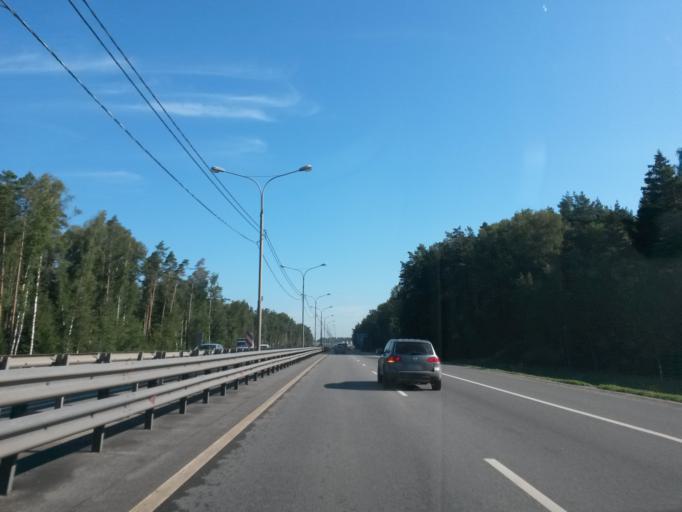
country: RU
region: Moskovskaya
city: Kostino
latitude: 56.0351
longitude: 37.8896
